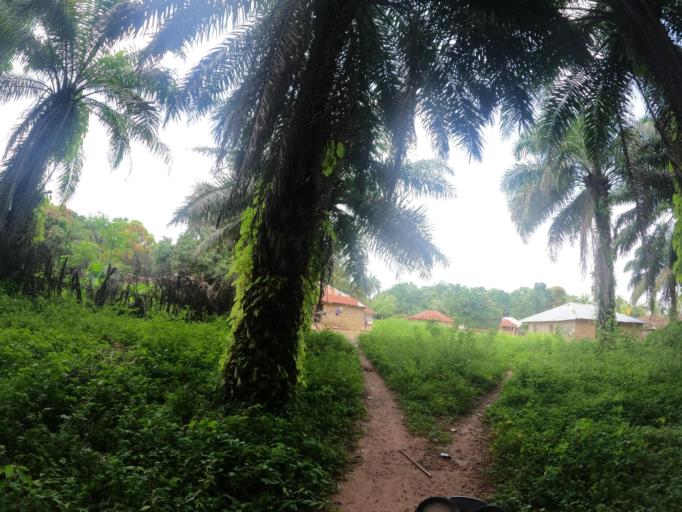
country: SL
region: Northern Province
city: Makeni
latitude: 9.1293
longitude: -12.2689
